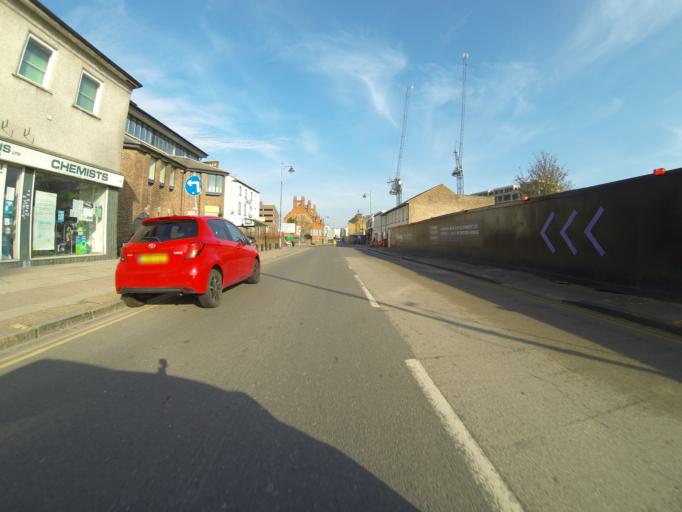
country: GB
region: England
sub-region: Kent
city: Dartford
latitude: 51.4419
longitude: 0.2159
